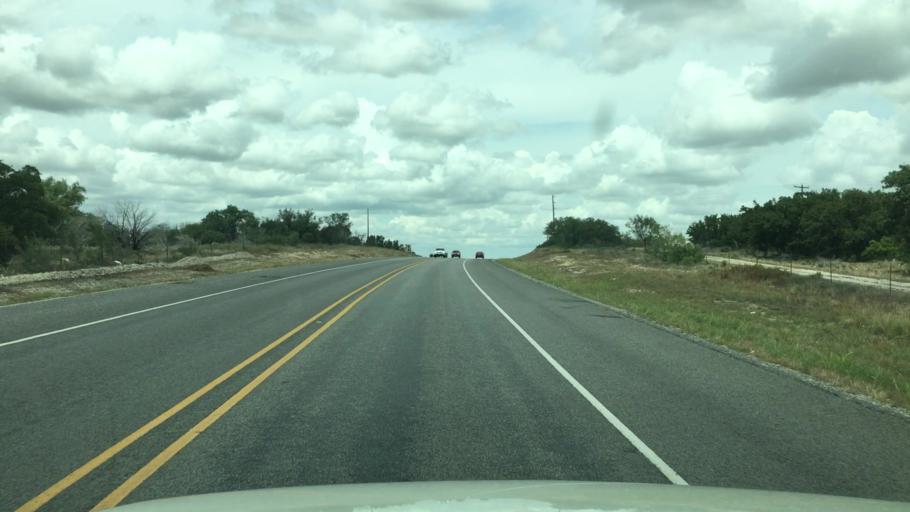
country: US
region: Texas
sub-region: McCulloch County
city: Brady
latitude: 31.0332
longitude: -99.2335
